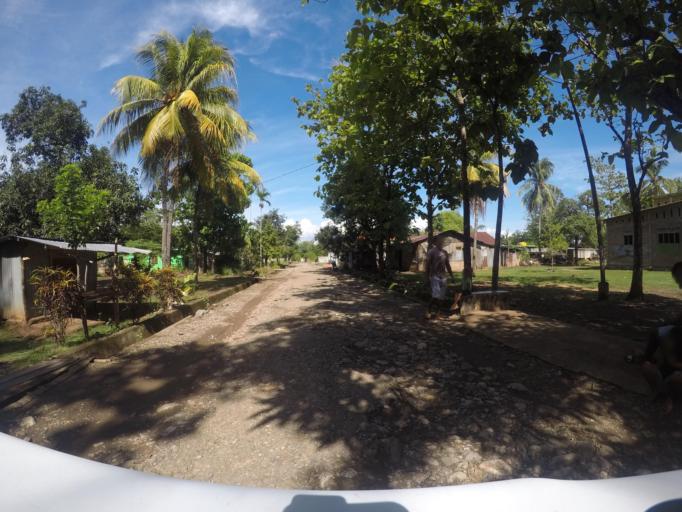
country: TL
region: Bobonaro
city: Maliana
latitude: -8.9878
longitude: 125.2039
